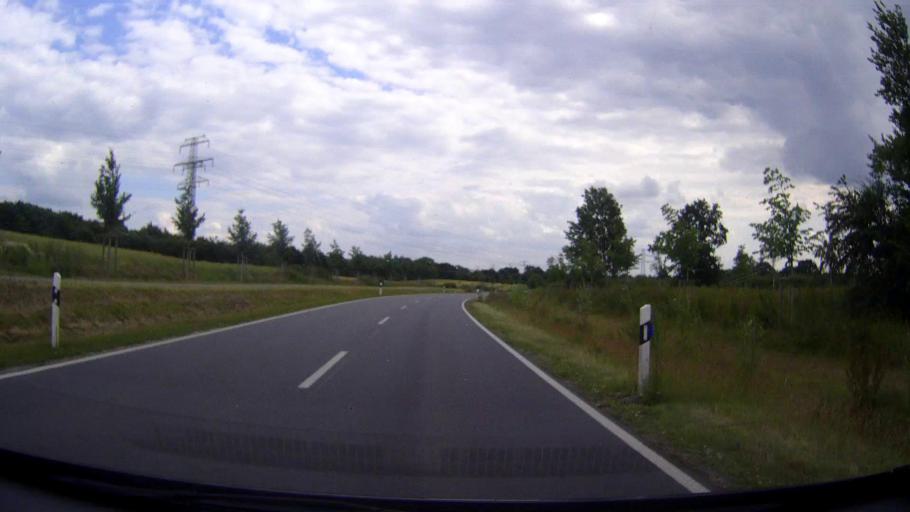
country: DE
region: Schleswig-Holstein
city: Badendorf
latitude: 53.8836
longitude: 10.6041
